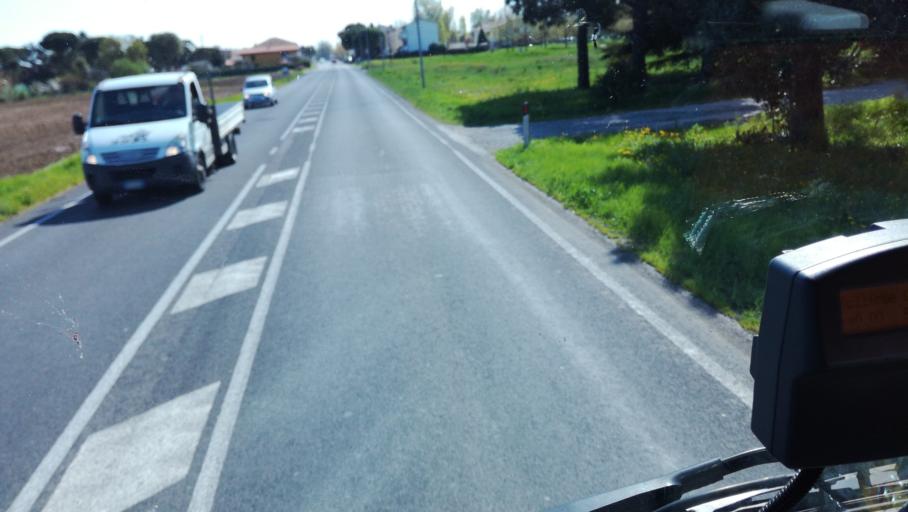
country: IT
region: Emilia-Romagna
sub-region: Provincia di Ravenna
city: Faenza
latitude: 44.3008
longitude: 11.8726
